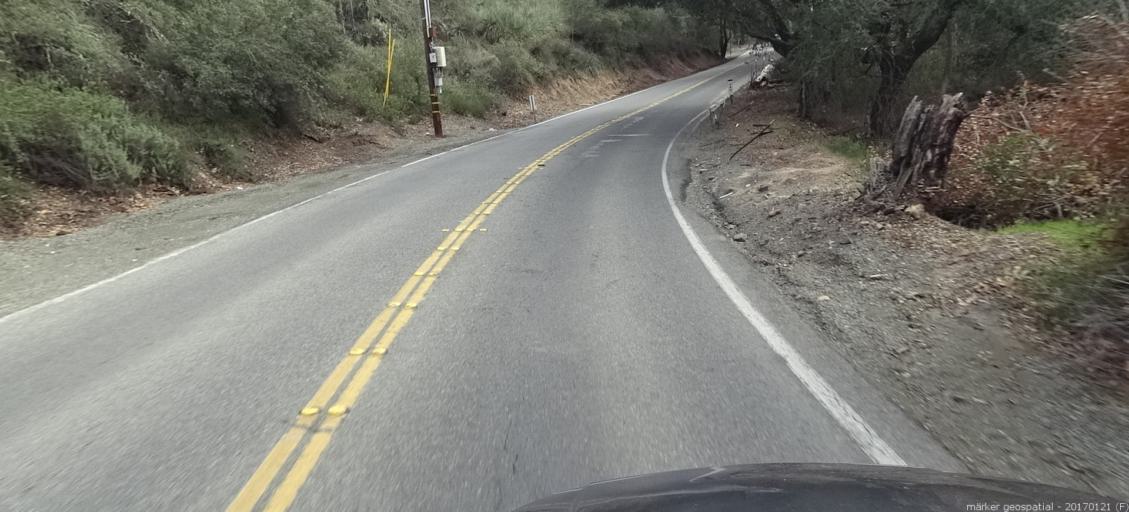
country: US
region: California
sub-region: Orange County
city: Trabuco Canyon
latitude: 33.6694
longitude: -117.6020
